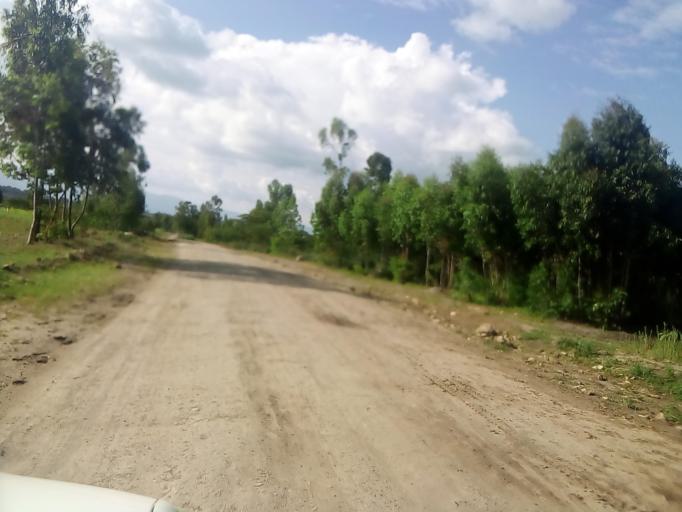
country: ET
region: Southern Nations, Nationalities, and People's Region
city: K'olito
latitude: 7.6472
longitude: 38.0521
